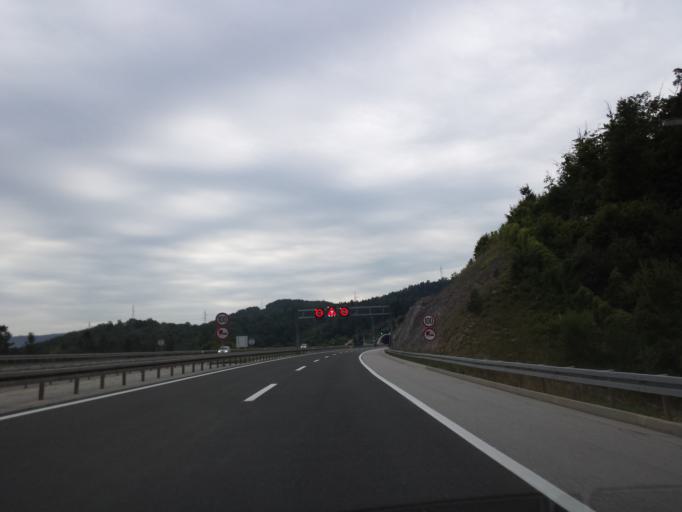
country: HR
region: Licko-Senjska
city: Otocac
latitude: 44.7866
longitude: 15.3356
